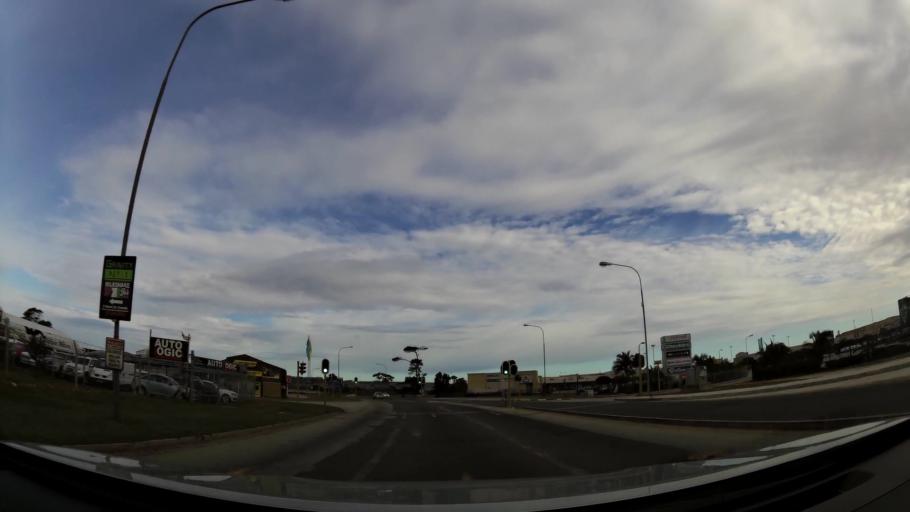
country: ZA
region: Eastern Cape
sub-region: Nelson Mandela Bay Metropolitan Municipality
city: Port Elizabeth
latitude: -33.9449
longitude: 25.5108
